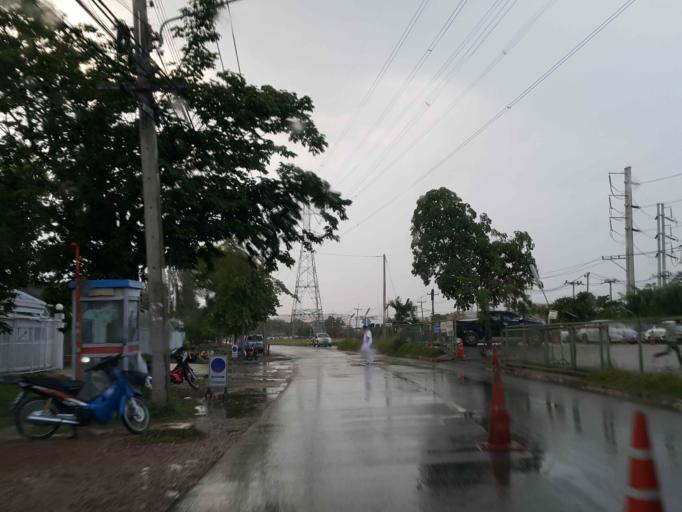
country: TH
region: Lamphun
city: Lamphun
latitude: 18.5903
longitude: 99.0520
